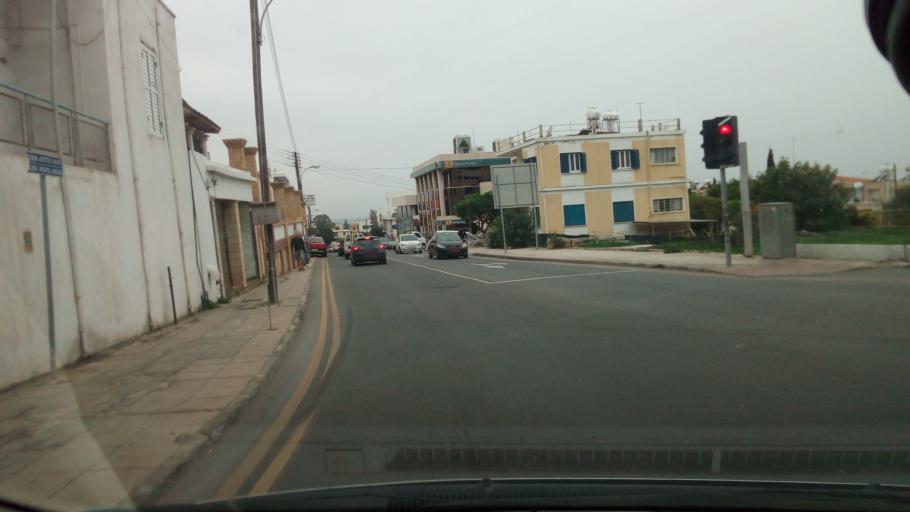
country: CY
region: Pafos
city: Paphos
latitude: 34.7742
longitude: 32.4194
